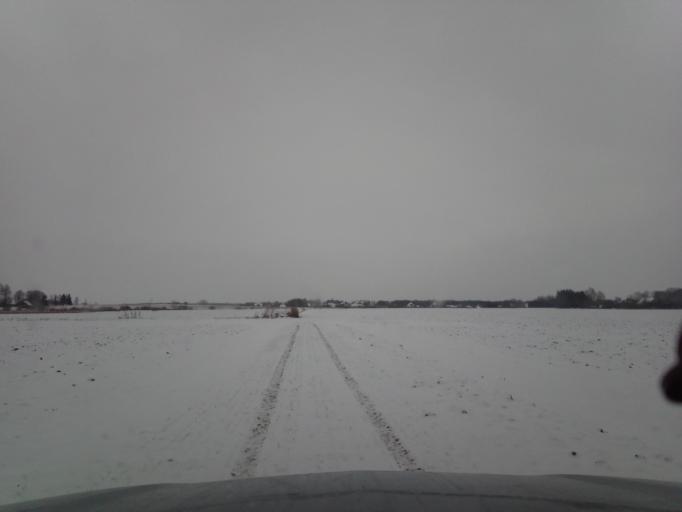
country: LT
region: Panevezys
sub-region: Panevezys City
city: Panevezys
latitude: 55.6233
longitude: 24.3386
